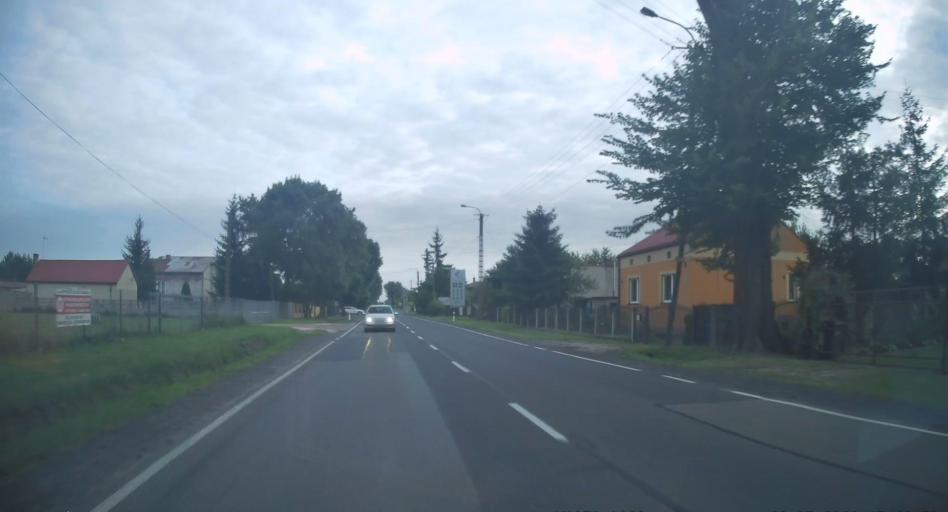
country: PL
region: Lodz Voivodeship
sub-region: Powiat radomszczanski
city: Radomsko
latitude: 51.1045
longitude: 19.4642
